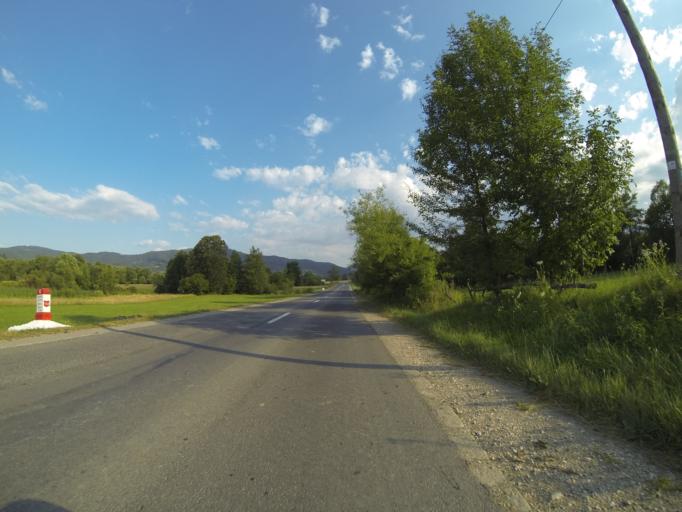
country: RO
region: Brasov
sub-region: Comuna Sinca Noua
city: Sinca Noua
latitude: 45.7222
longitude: 25.2392
